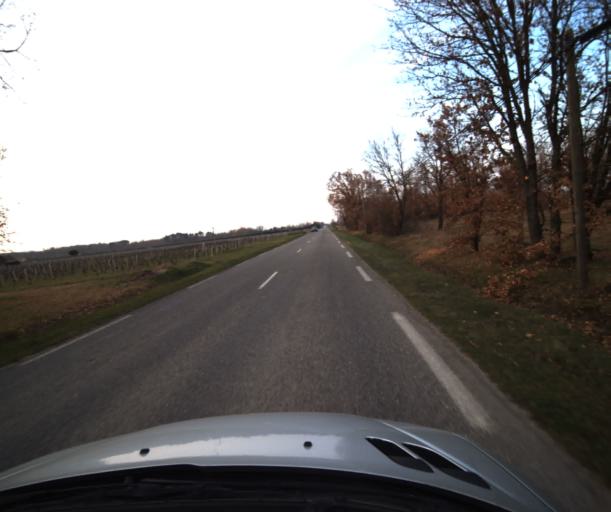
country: FR
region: Midi-Pyrenees
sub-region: Departement de la Haute-Garonne
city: Fronton
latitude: 43.8577
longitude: 1.3844
